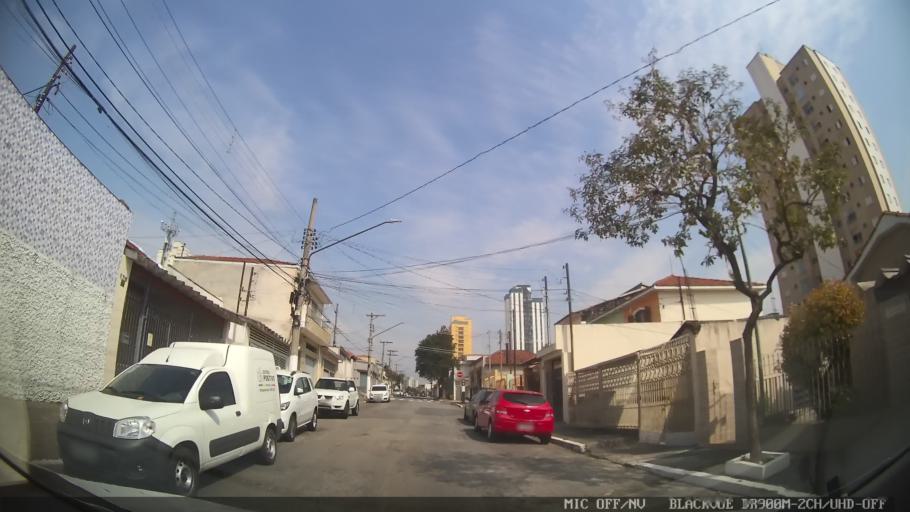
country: BR
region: Sao Paulo
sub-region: Sao Caetano Do Sul
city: Sao Caetano do Sul
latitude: -23.6091
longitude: -46.6032
